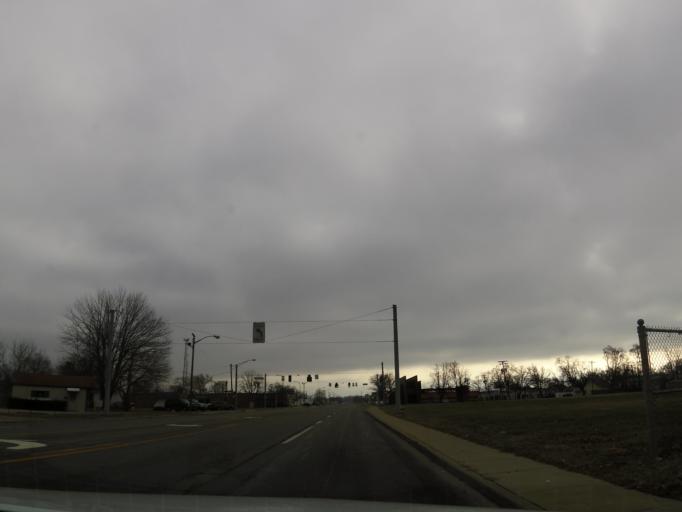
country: US
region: Indiana
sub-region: Bartholomew County
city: Columbus
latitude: 39.1969
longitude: -85.9026
